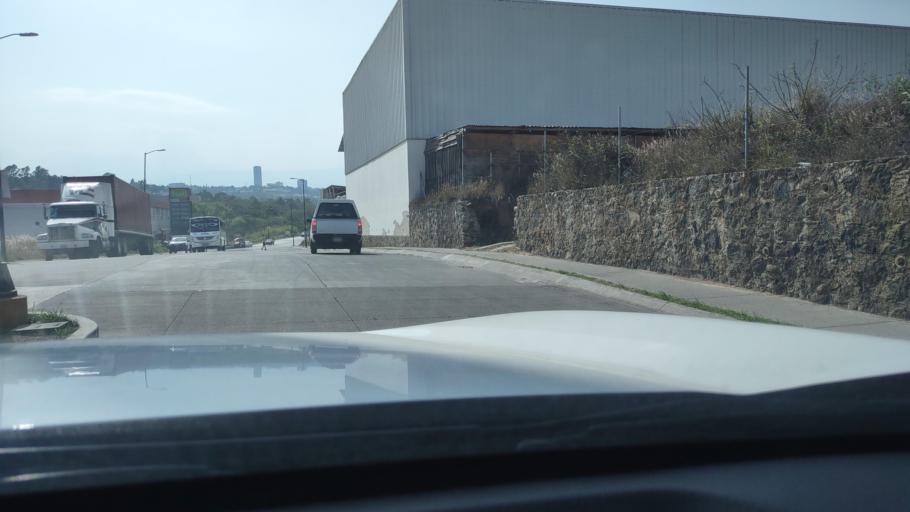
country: MX
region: Veracruz
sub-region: Emiliano Zapata
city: Las Trancas
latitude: 19.5128
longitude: -96.8507
